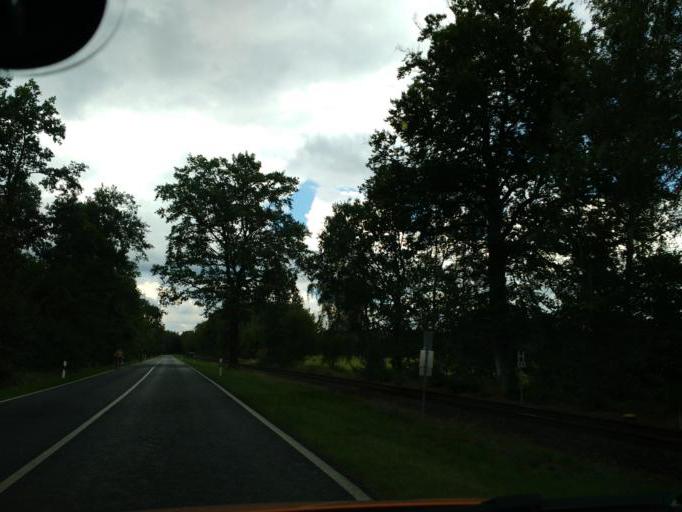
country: DE
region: Brandenburg
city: Wandlitz
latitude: 52.8159
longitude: 13.4984
